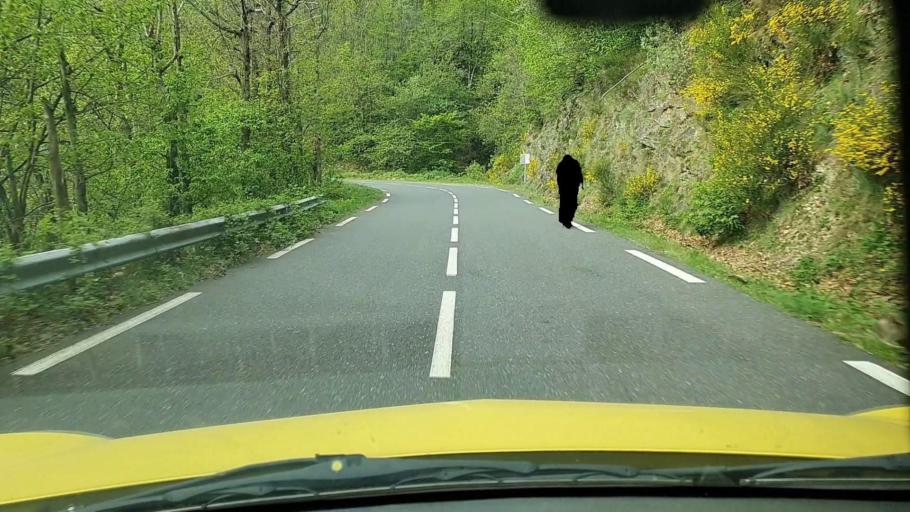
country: FR
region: Languedoc-Roussillon
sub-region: Departement du Gard
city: Valleraugue
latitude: 44.0875
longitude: 3.5779
